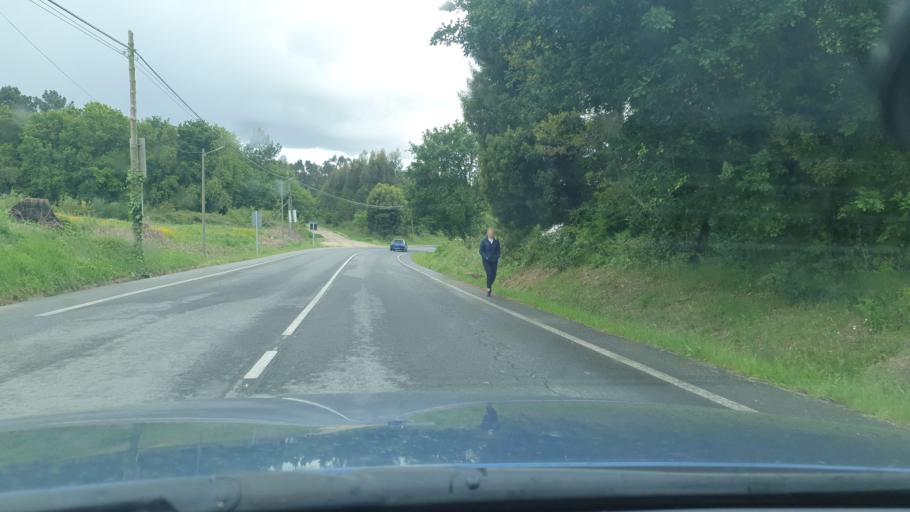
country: ES
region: Galicia
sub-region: Provincia da Coruna
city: Santiago de Compostela
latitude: 42.8426
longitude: -8.5825
